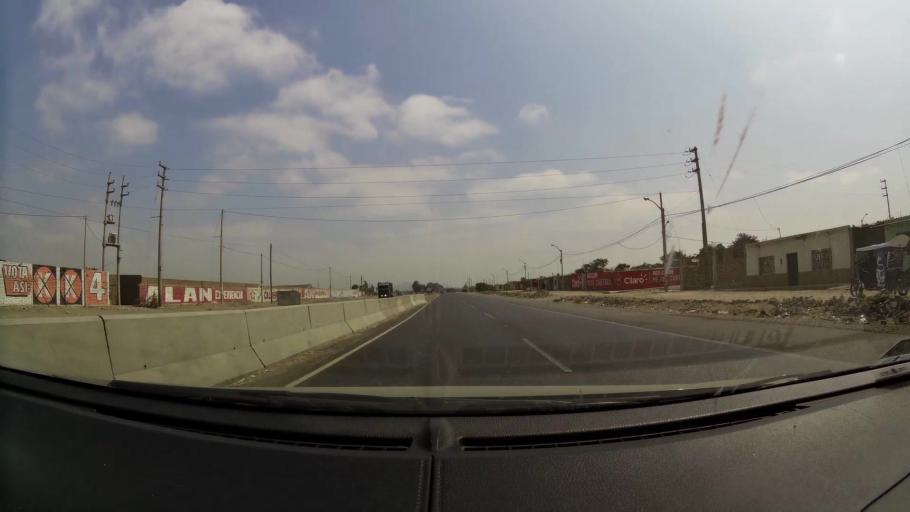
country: PE
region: La Libertad
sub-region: Ascope
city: Chicama
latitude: -7.8662
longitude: -79.1369
